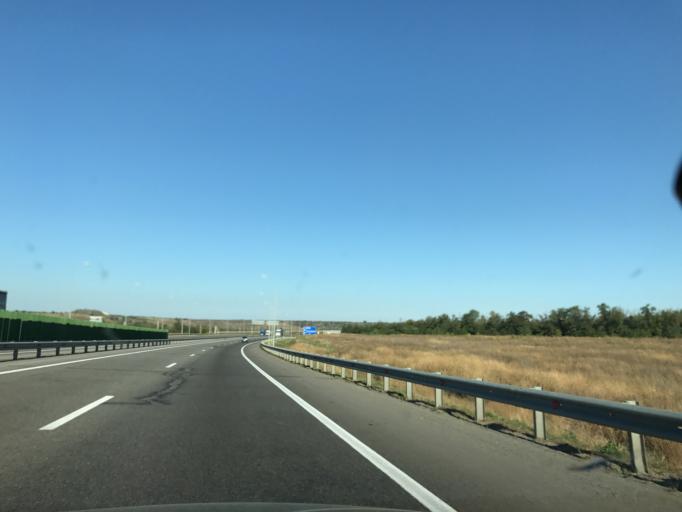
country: RU
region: Rostov
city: Tarasovskiy
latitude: 48.7488
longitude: 40.3815
